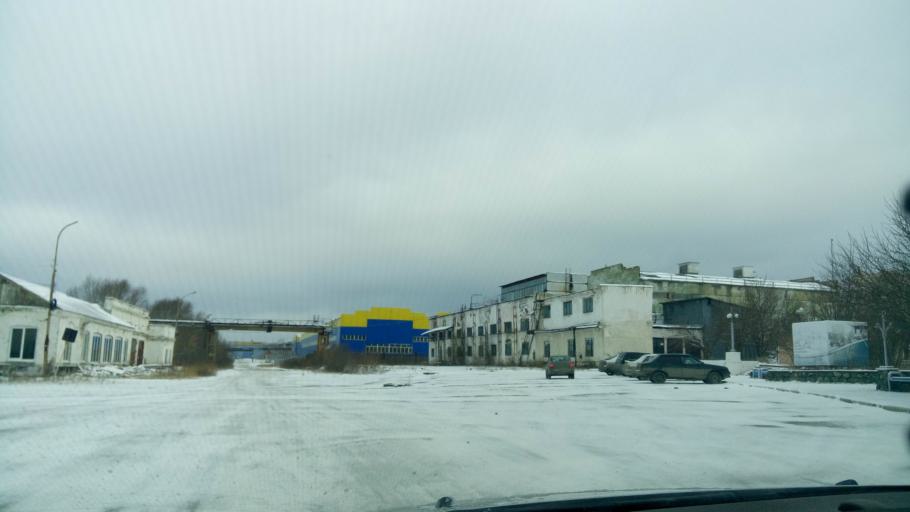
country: RU
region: Sverdlovsk
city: Polevskoy
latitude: 56.4679
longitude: 60.1783
